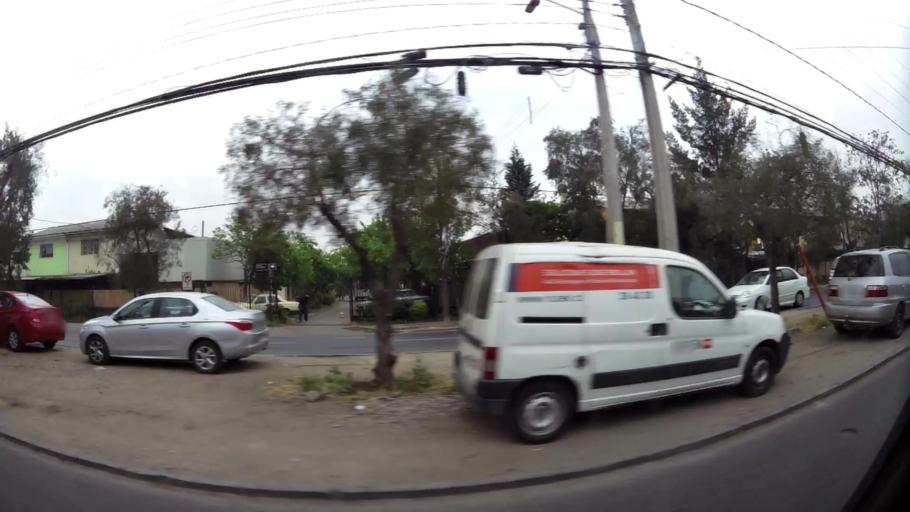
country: CL
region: Santiago Metropolitan
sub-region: Provincia de Santiago
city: Santiago
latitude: -33.4787
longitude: -70.6657
